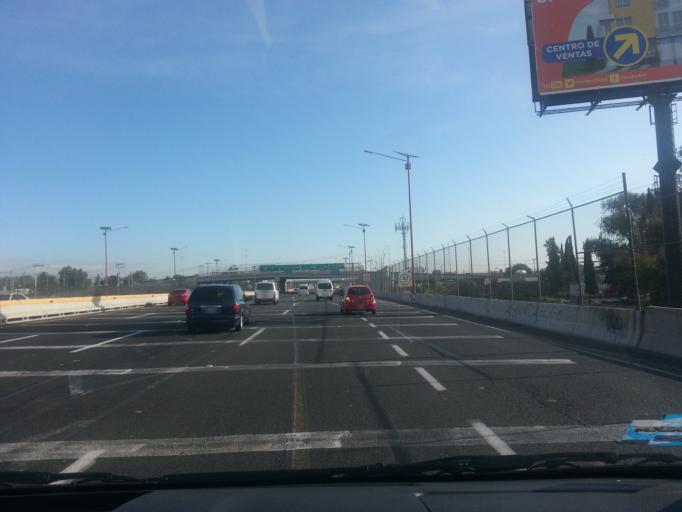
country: MX
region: Mexico
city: Ecatepec
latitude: 19.5986
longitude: -99.0394
